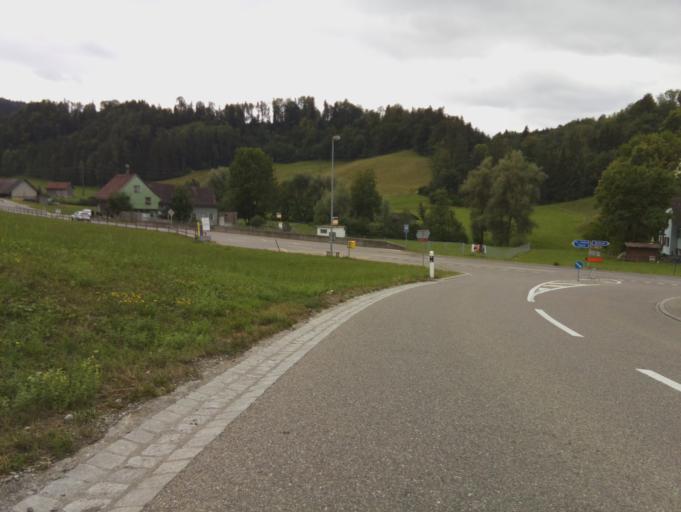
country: CH
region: Saint Gallen
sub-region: Wahlkreis Wil
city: Jonschwil
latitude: 47.4095
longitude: 9.0900
